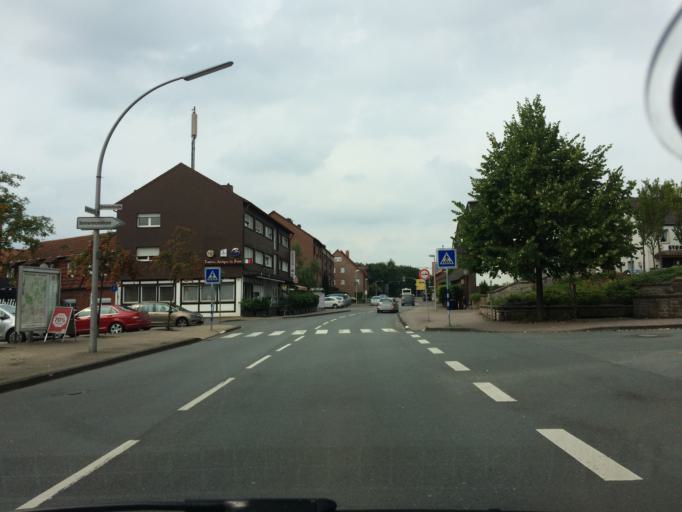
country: DE
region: North Rhine-Westphalia
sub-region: Regierungsbezirk Munster
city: Klein Reken
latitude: 51.7586
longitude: 6.9994
